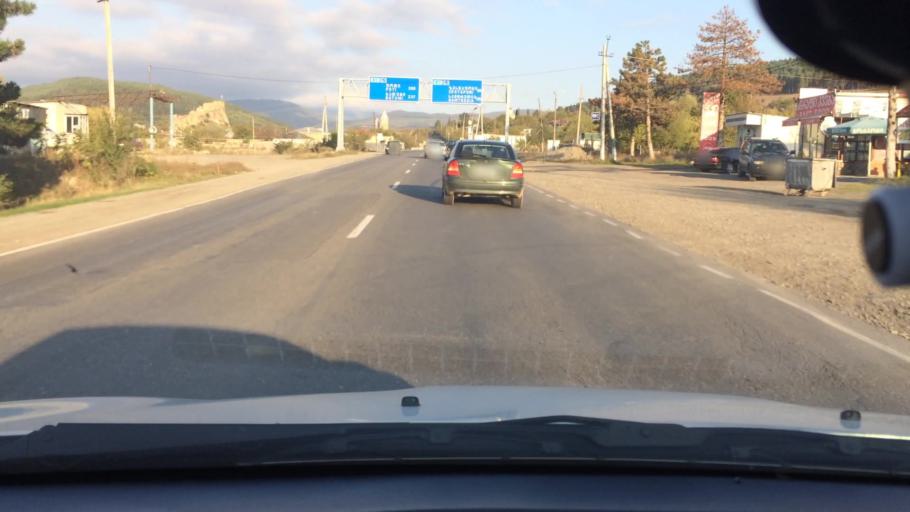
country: GE
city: Surami
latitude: 42.0138
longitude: 43.5750
